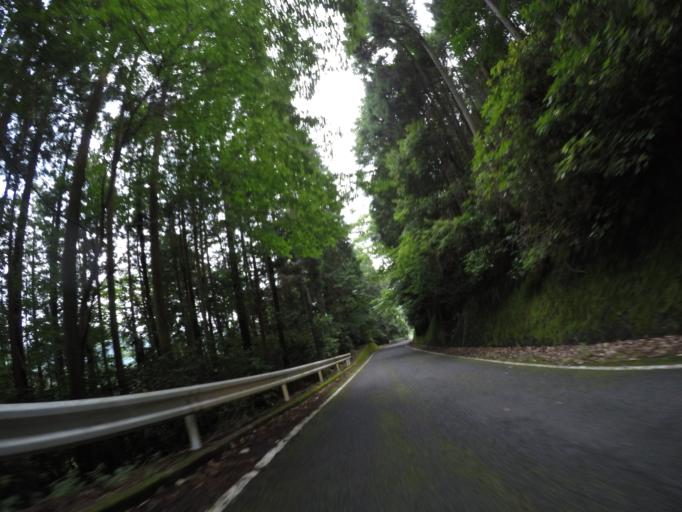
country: JP
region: Shizuoka
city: Fujinomiya
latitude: 35.2357
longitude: 138.5592
